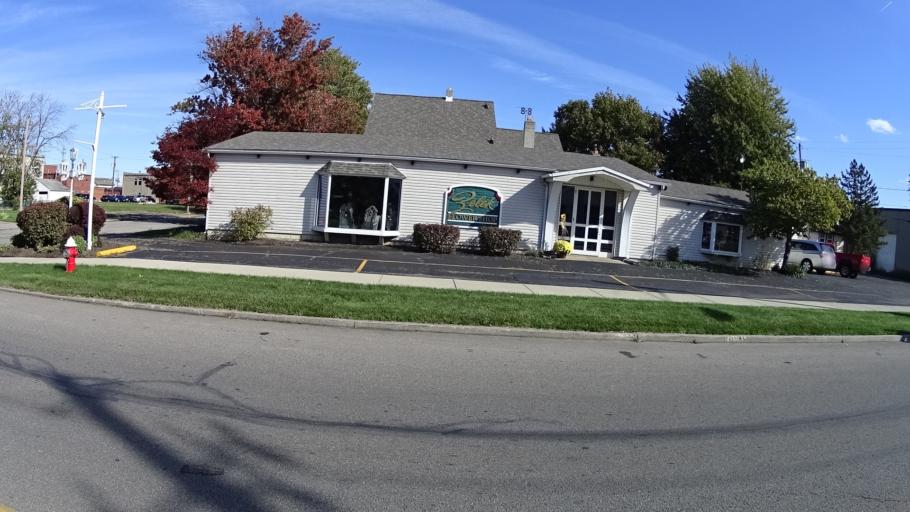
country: US
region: Ohio
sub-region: Lorain County
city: Lorain
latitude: 41.4613
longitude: -82.1738
